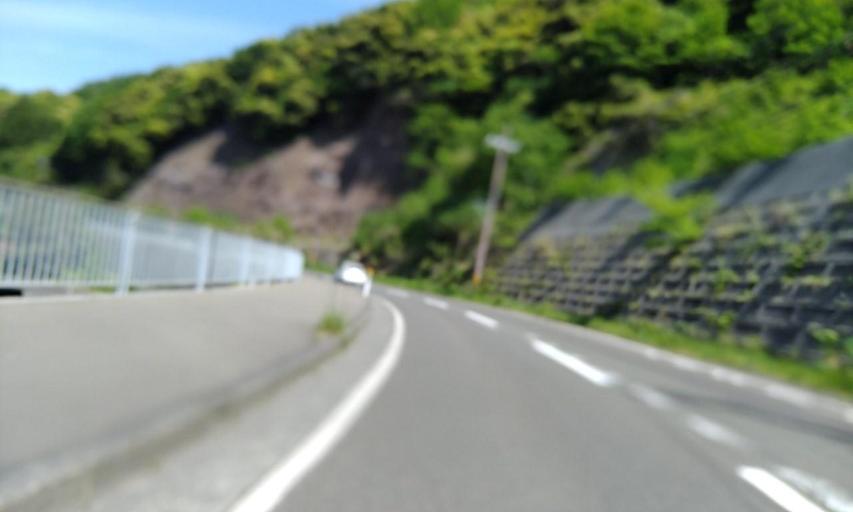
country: JP
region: Fukui
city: Obama
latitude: 35.5297
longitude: 135.7917
